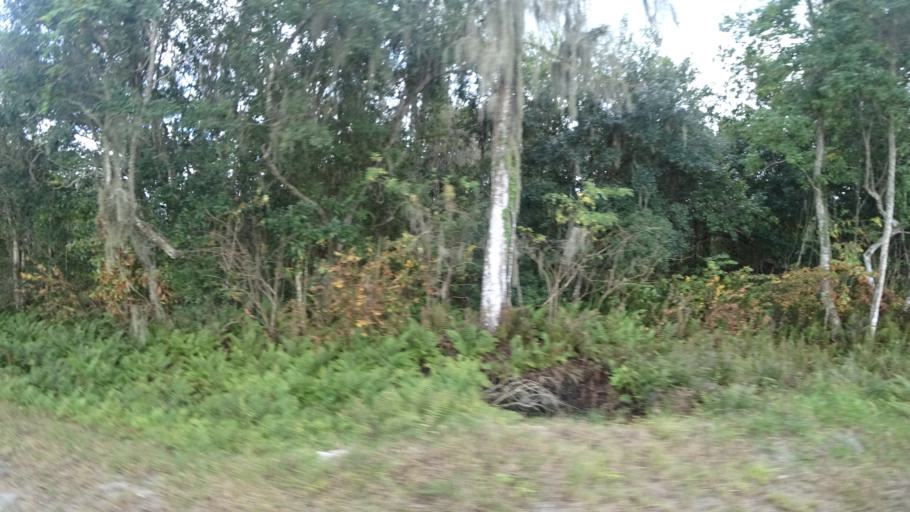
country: US
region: Florida
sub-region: Sarasota County
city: Lake Sarasota
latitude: 27.4010
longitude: -82.2527
